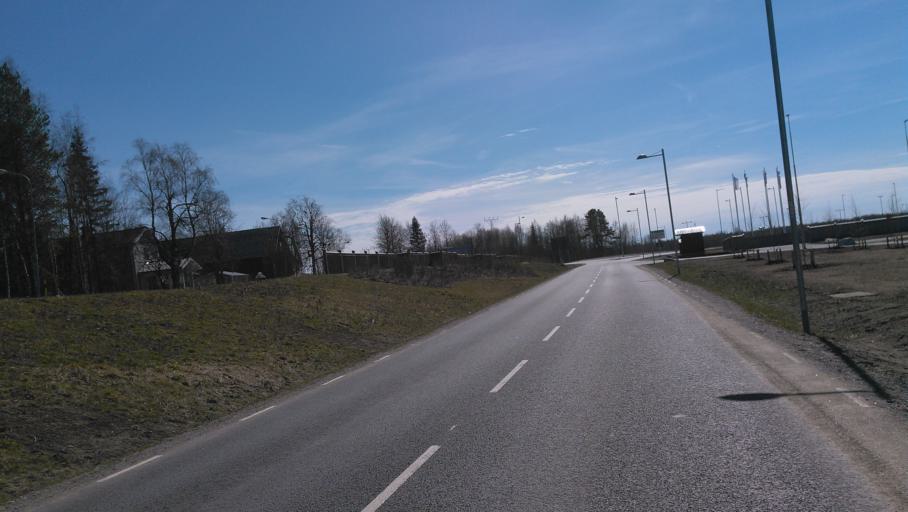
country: SE
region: Vaesterbotten
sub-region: Umea Kommun
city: Umea
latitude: 63.8064
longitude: 20.2574
